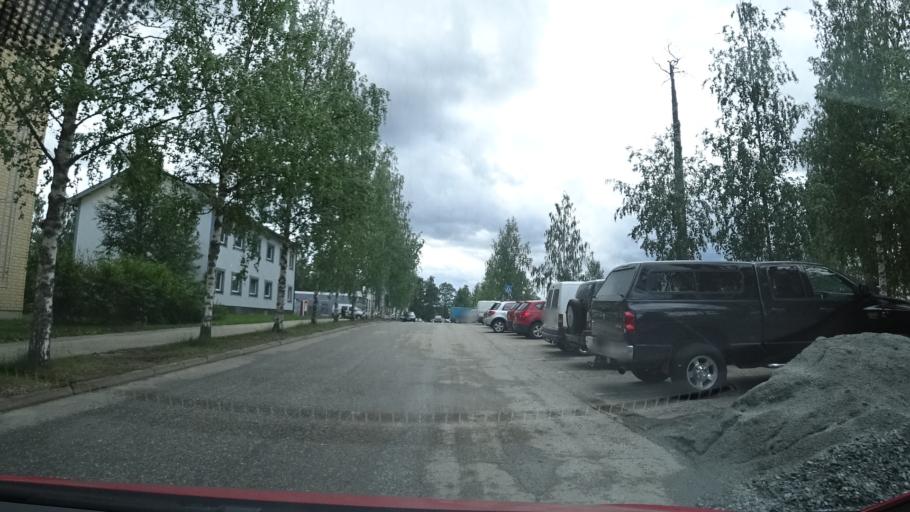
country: FI
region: North Karelia
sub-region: Pielisen Karjala
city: Nurmes
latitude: 63.5429
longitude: 29.1423
